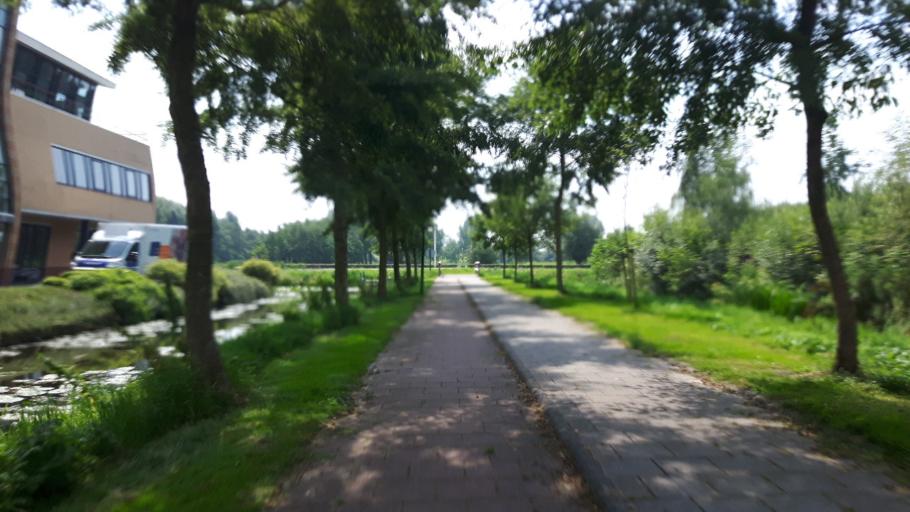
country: NL
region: Utrecht
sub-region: Gemeente Lopik
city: Lopik
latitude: 51.9705
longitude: 4.9414
